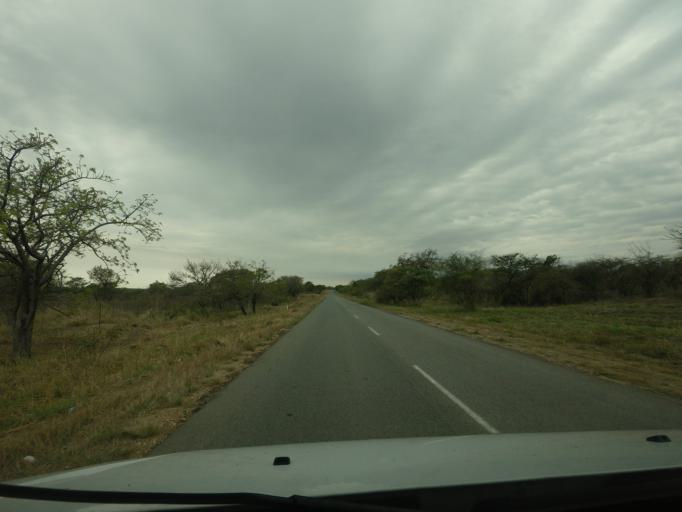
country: ZA
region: Limpopo
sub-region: Mopani District Municipality
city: Hoedspruit
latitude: -24.5069
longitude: 30.9197
